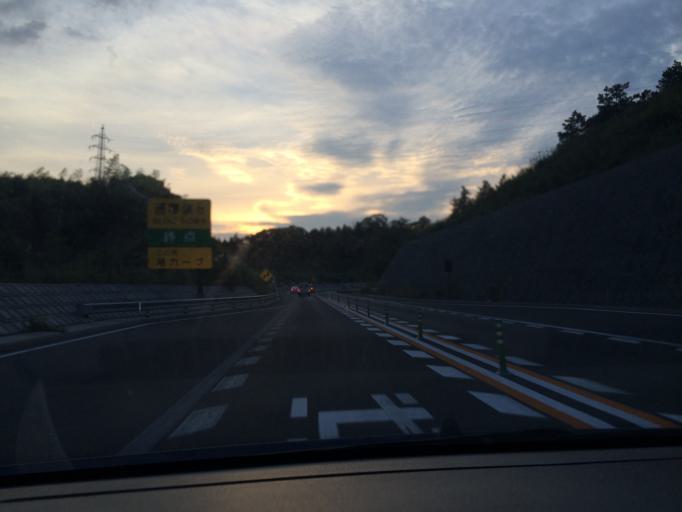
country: JP
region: Shimane
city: Izumo
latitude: 35.3260
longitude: 132.7189
